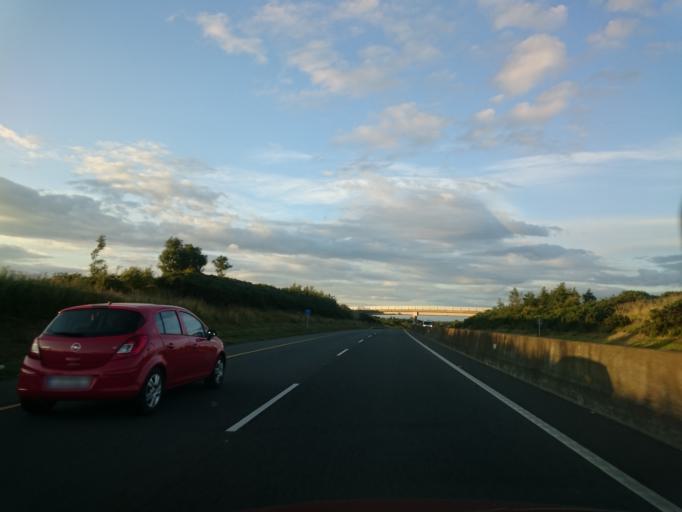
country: IE
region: Leinster
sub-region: Loch Garman
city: Castletown
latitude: 52.7339
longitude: -6.2364
